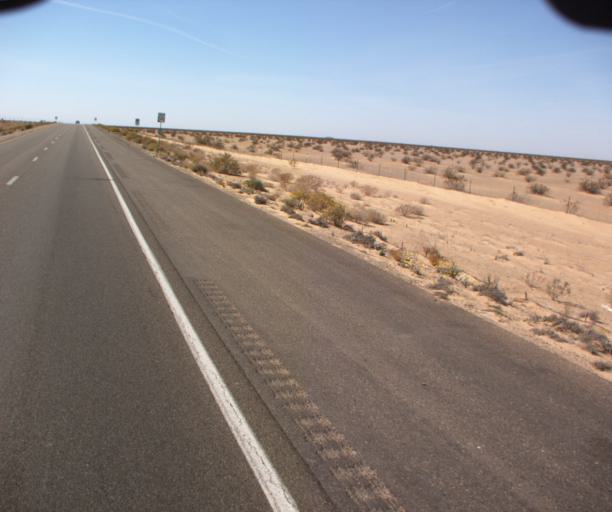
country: US
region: Arizona
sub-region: Yuma County
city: Somerton
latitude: 32.4968
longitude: -114.6490
